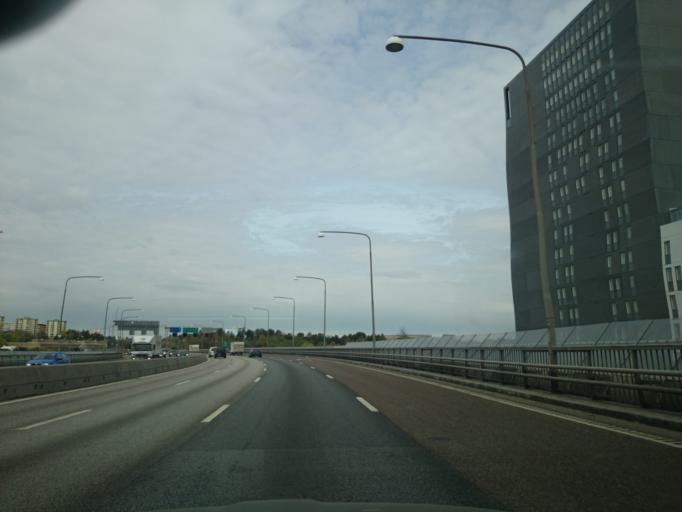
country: SE
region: Stockholm
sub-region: Solna Kommun
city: Solna
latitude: 59.3395
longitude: 18.0113
